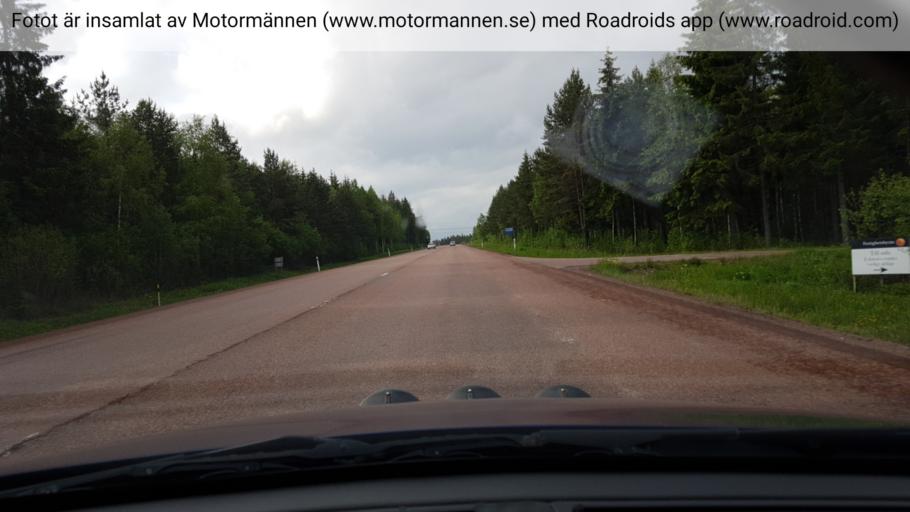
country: SE
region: Dalarna
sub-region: Mora Kommun
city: Mora
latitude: 61.0276
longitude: 14.5902
